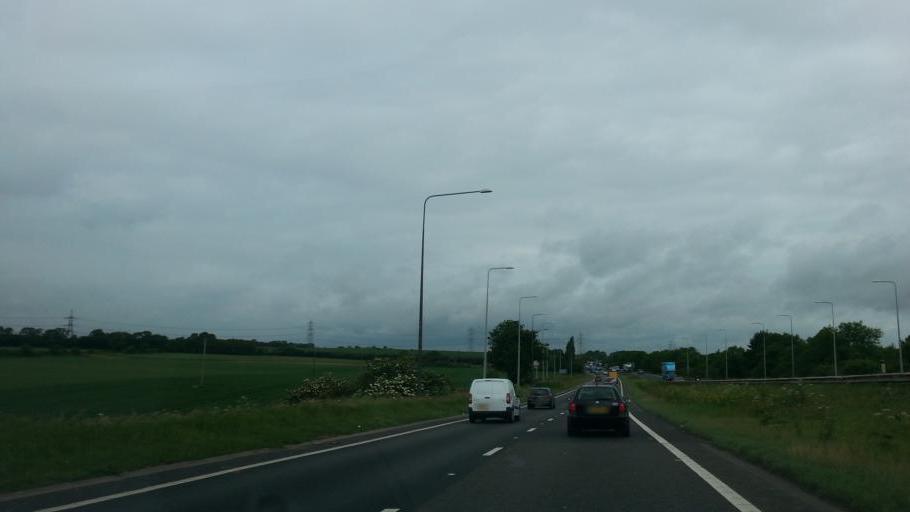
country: GB
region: England
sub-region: City and Borough of Wakefield
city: North Elmsall
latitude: 53.6202
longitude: -1.2327
